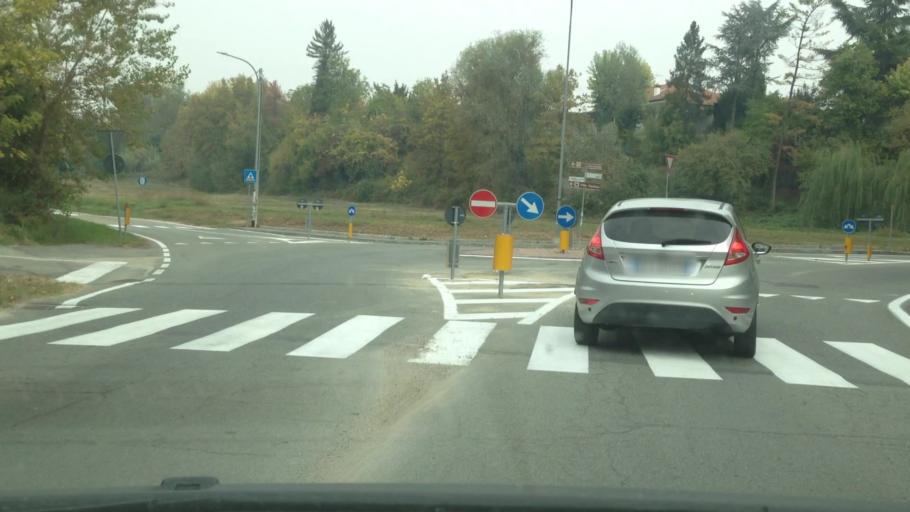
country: IT
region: Piedmont
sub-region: Provincia di Asti
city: Asti
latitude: 44.9153
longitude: 8.1978
